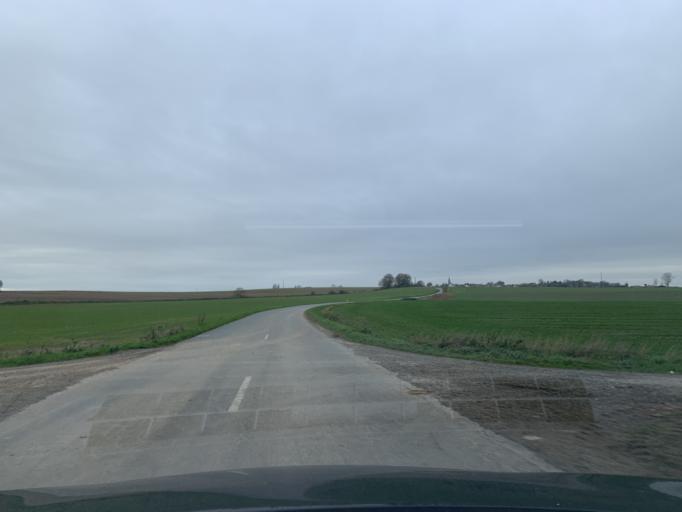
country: FR
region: Nord-Pas-de-Calais
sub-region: Departement du Pas-de-Calais
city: Oisy-le-Verger
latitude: 50.2413
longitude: 3.1427
